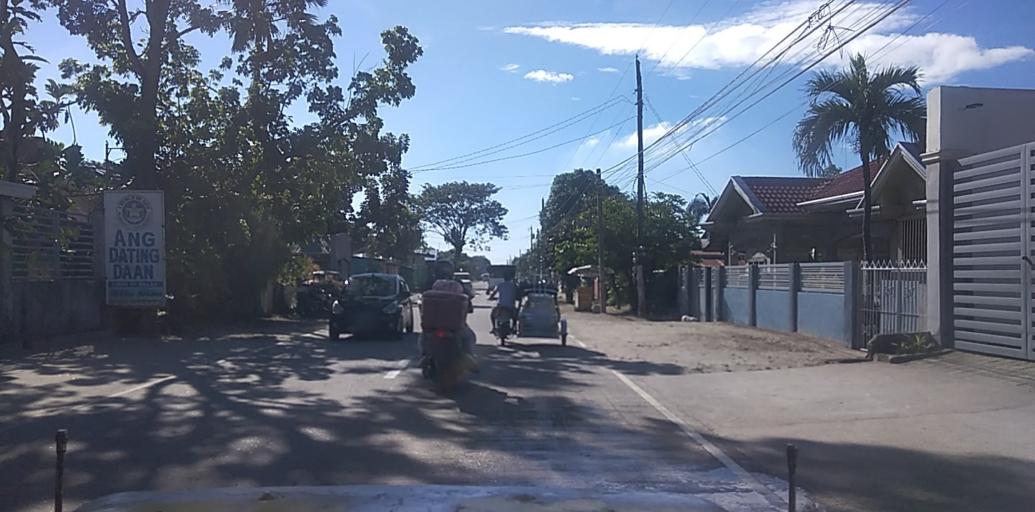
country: PH
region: Central Luzon
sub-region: Province of Pampanga
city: San Patricio
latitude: 15.0835
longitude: 120.7158
